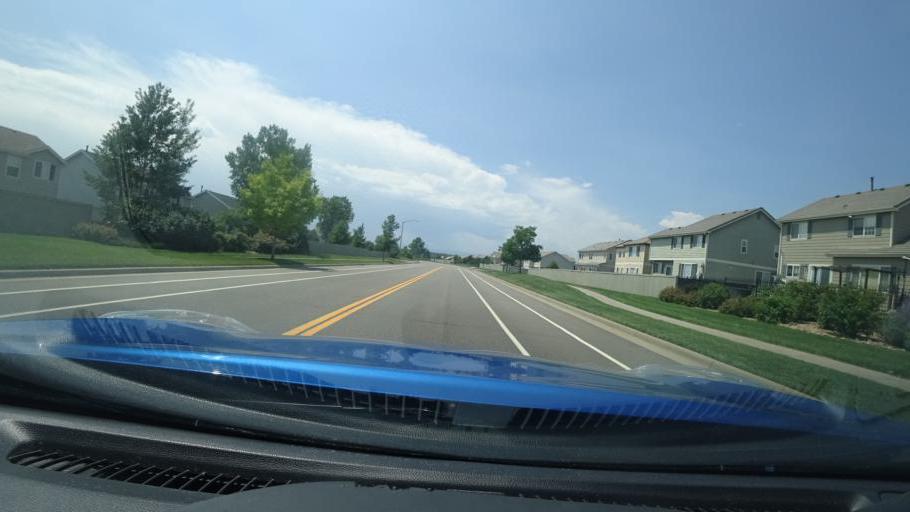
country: US
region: Colorado
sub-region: Adams County
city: Aurora
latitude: 39.6726
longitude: -104.7647
